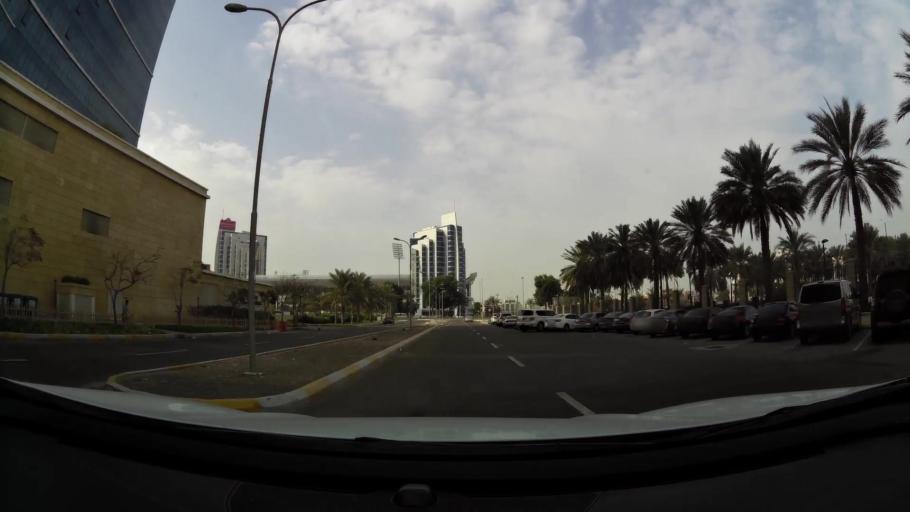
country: AE
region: Abu Dhabi
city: Abu Dhabi
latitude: 24.4558
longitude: 54.3947
